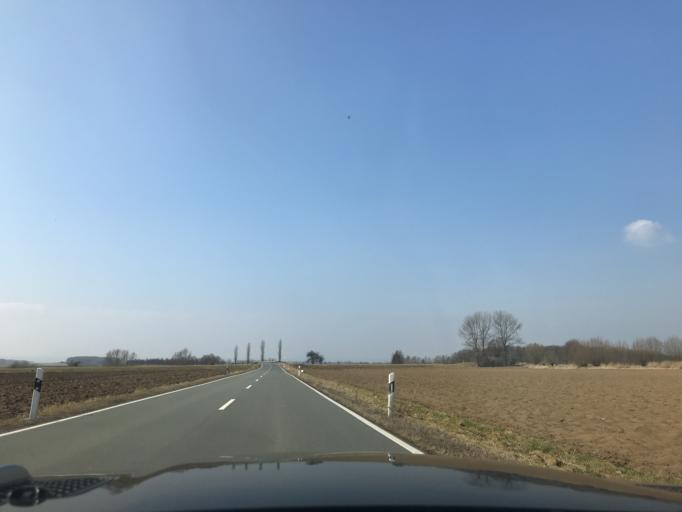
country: DE
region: Thuringia
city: Bad Langensalza
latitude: 51.1378
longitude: 10.6271
